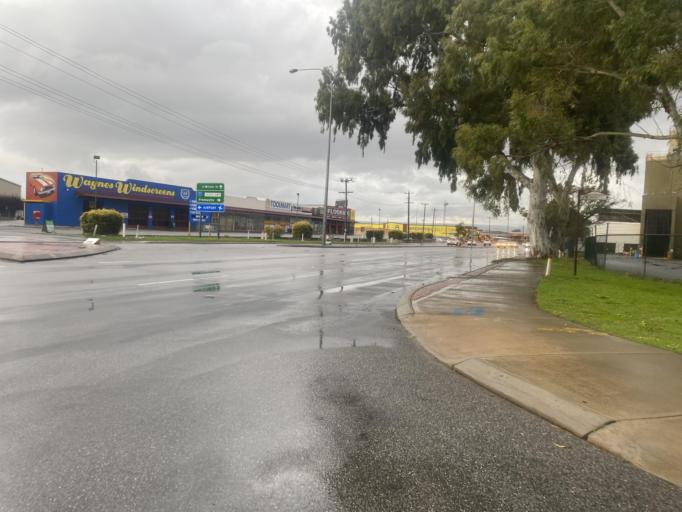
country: AU
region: Western Australia
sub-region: Canning
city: Bentley
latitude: -31.9944
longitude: 115.9272
